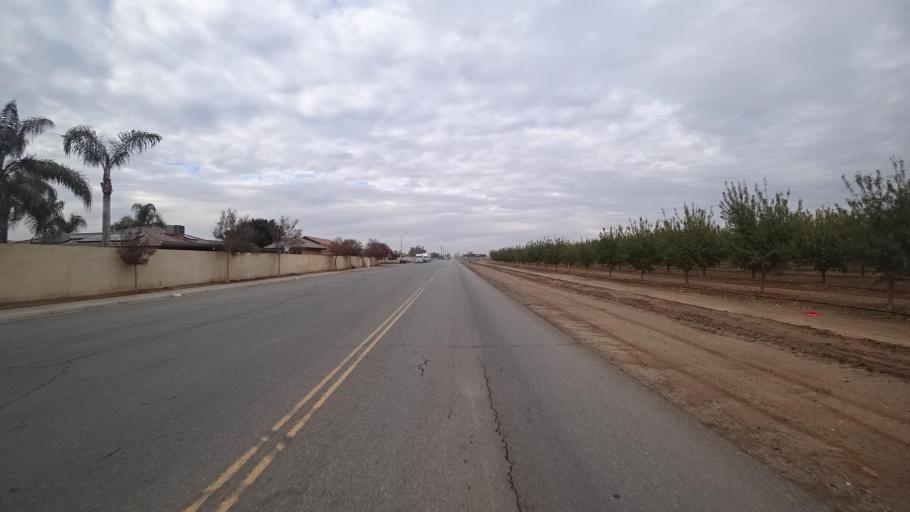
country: US
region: California
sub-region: Kern County
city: Arvin
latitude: 35.1896
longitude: -118.8241
